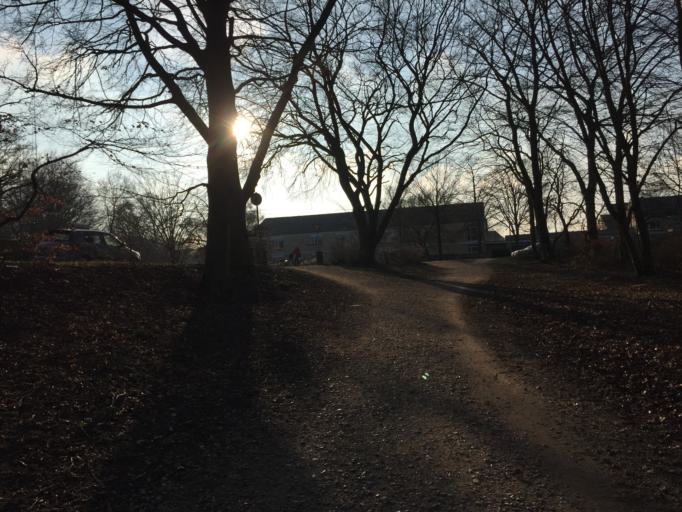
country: DK
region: South Denmark
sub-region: Odense Kommune
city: Odense
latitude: 55.3868
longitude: 10.4079
